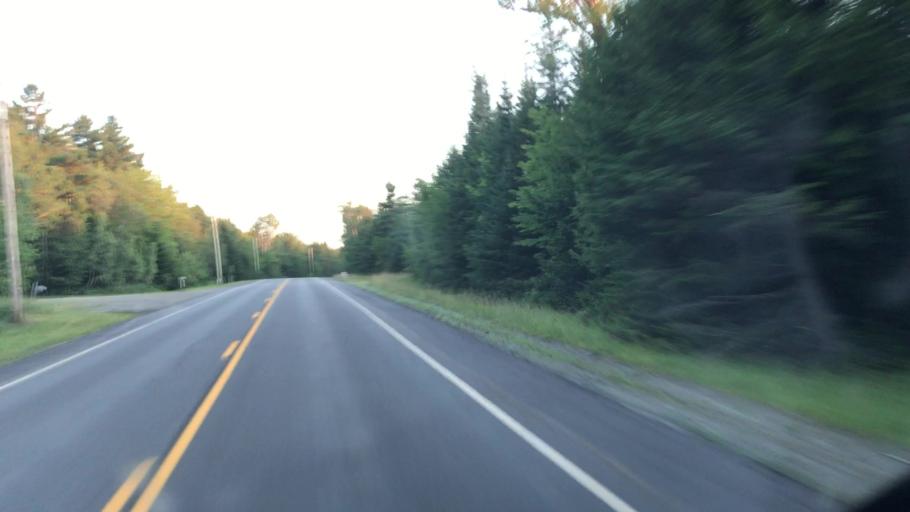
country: US
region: Maine
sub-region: Penobscot County
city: Medway
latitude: 45.5694
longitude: -68.3217
